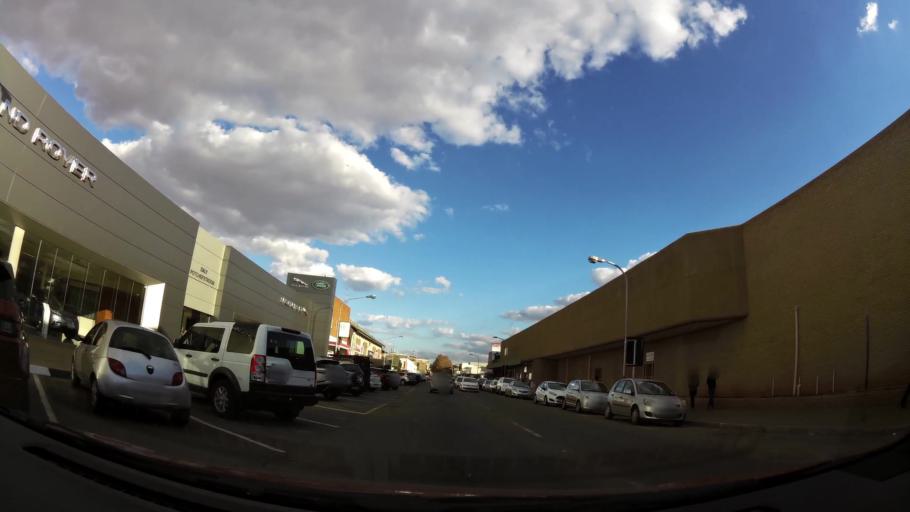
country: ZA
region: North-West
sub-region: Dr Kenneth Kaunda District Municipality
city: Potchefstroom
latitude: -26.7083
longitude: 27.0977
